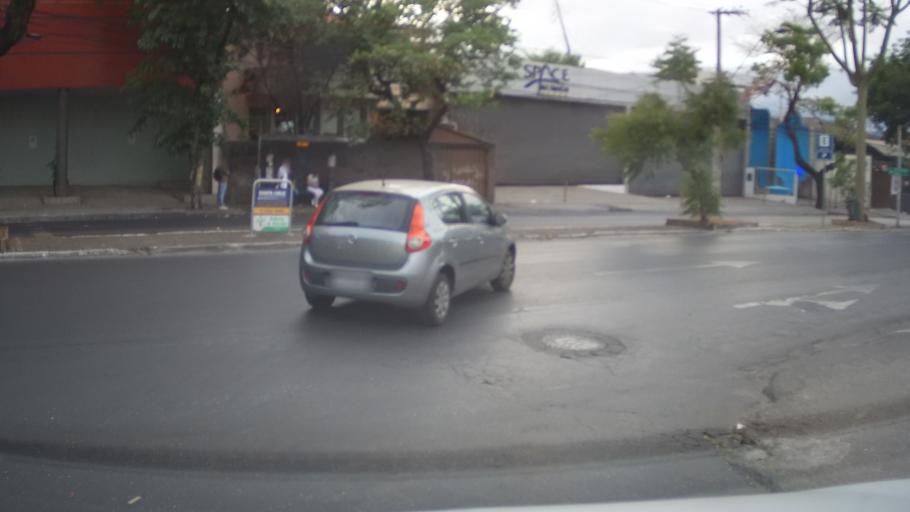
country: BR
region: Minas Gerais
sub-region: Belo Horizonte
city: Belo Horizonte
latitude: -19.9062
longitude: -43.9641
